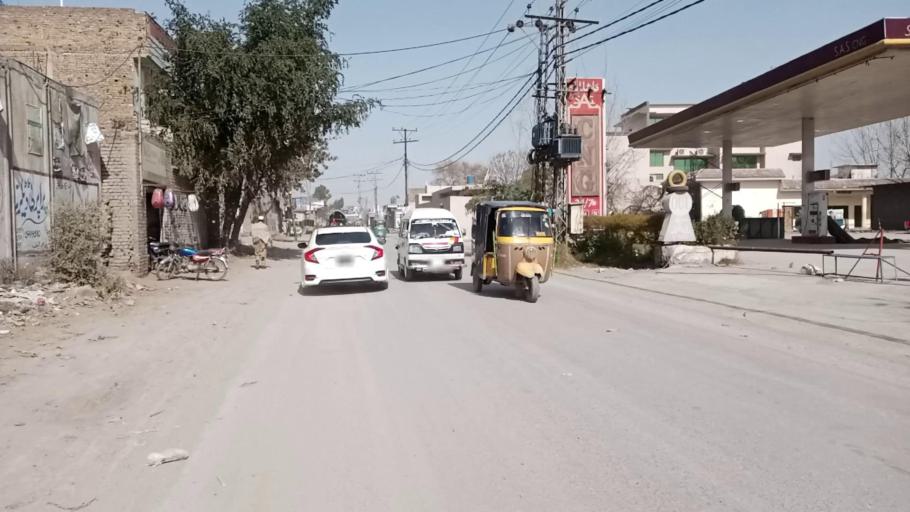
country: PK
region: Khyber Pakhtunkhwa
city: Peshawar
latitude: 34.0135
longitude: 71.6470
